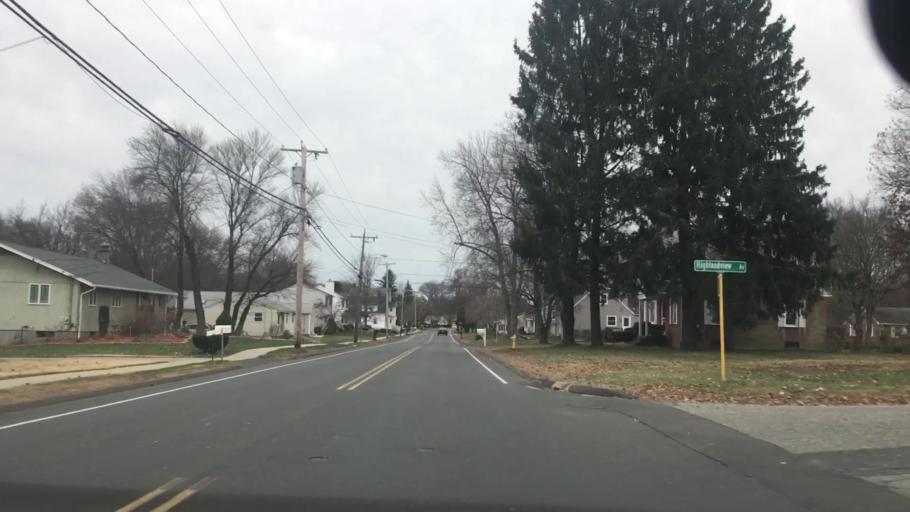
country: US
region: Massachusetts
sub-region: Hampden County
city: East Longmeadow
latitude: 42.0712
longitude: -72.5231
